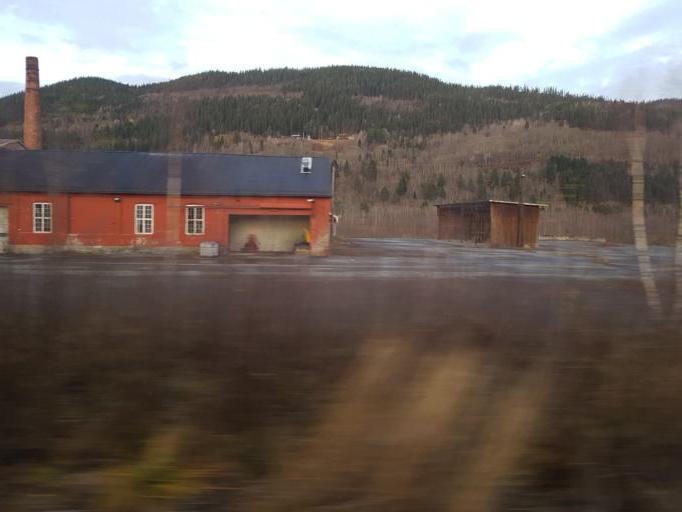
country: NO
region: Sor-Trondelag
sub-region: Melhus
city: Lundamo
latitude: 63.1572
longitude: 10.2911
